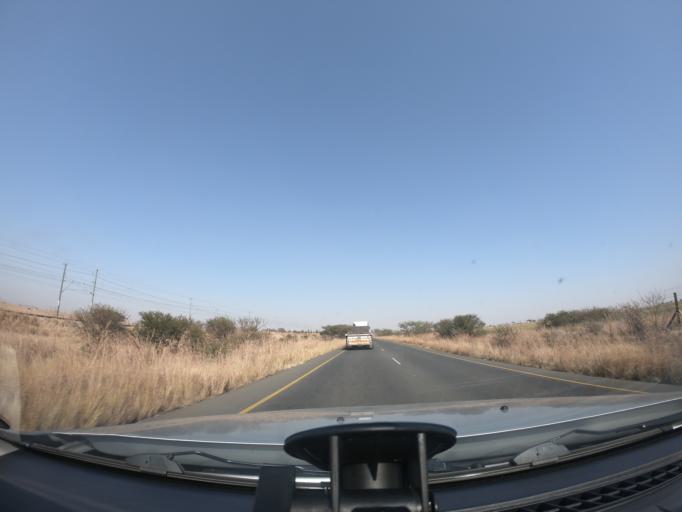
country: ZA
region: KwaZulu-Natal
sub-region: uThukela District Municipality
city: Ladysmith
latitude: -28.7620
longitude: 29.8193
